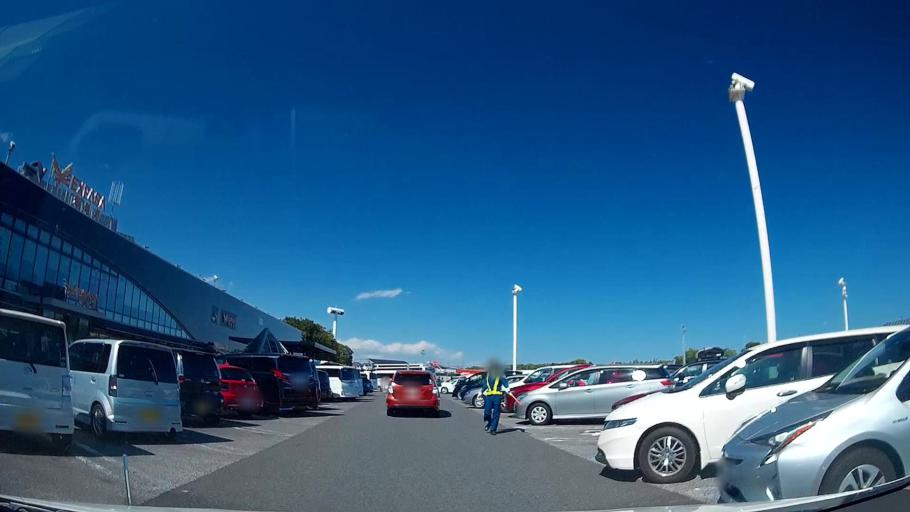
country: JP
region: Kanagawa
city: Atsugi
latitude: 35.4319
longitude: 139.3987
